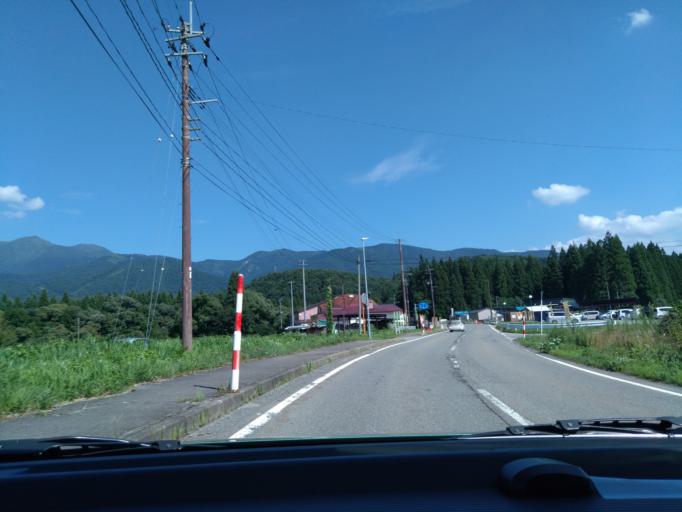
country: JP
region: Akita
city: Kakunodatemachi
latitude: 39.7404
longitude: 140.7130
